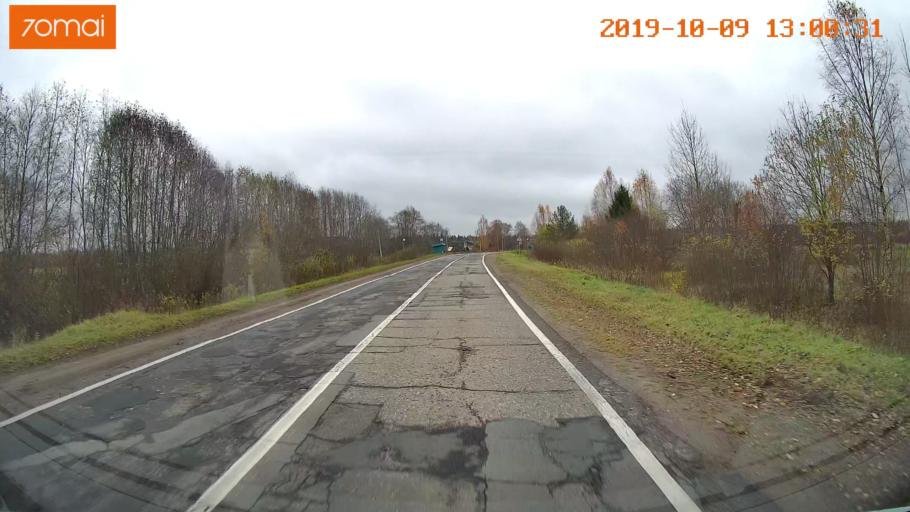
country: RU
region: Jaroslavl
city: Prechistoye
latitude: 58.3766
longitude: 40.4810
